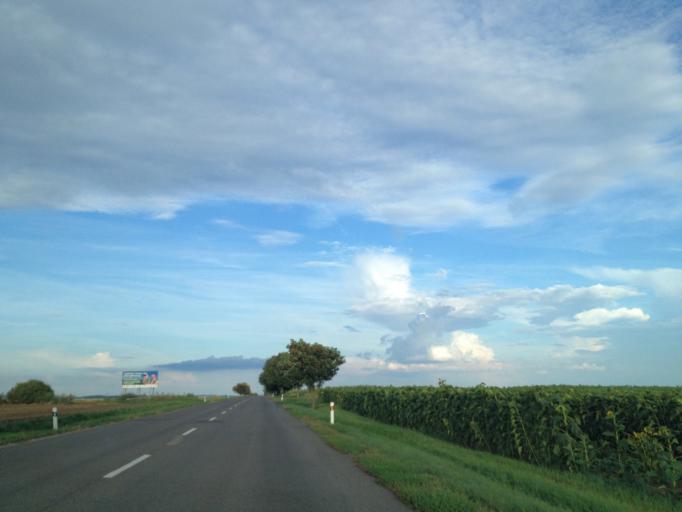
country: SK
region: Nitriansky
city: Svodin
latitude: 47.8942
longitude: 18.3902
